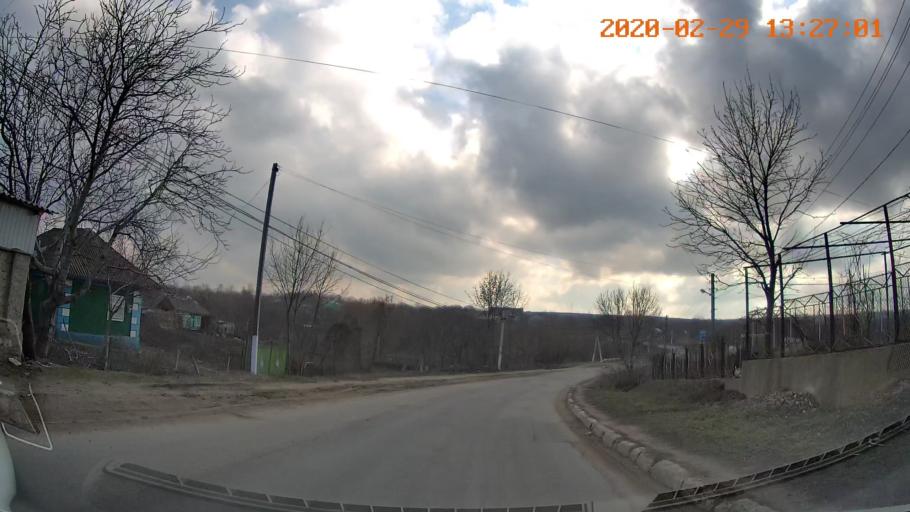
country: MD
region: Telenesti
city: Camenca
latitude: 47.9152
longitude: 28.6401
